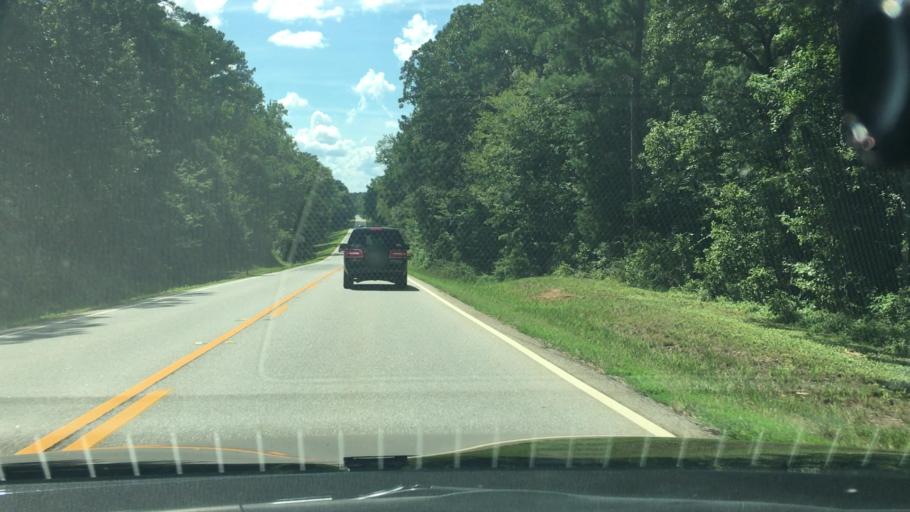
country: US
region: Georgia
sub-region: Putnam County
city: Eatonton
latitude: 33.3113
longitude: -83.5304
